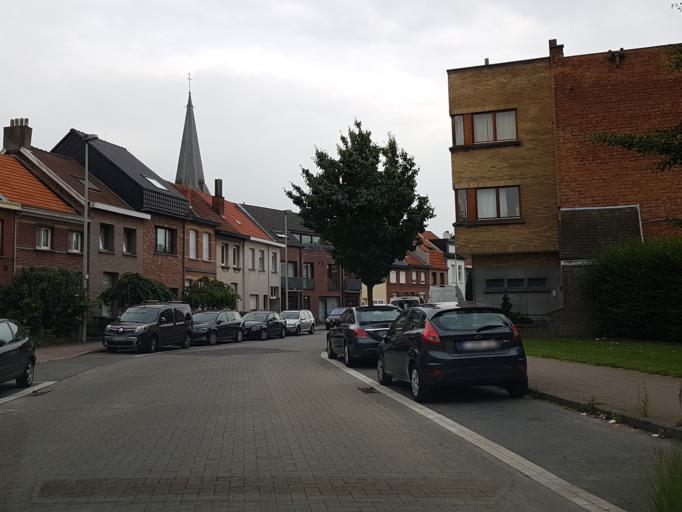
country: BE
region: Flanders
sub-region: Provincie Antwerpen
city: Borsbeek
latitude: 51.2065
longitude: 4.4634
